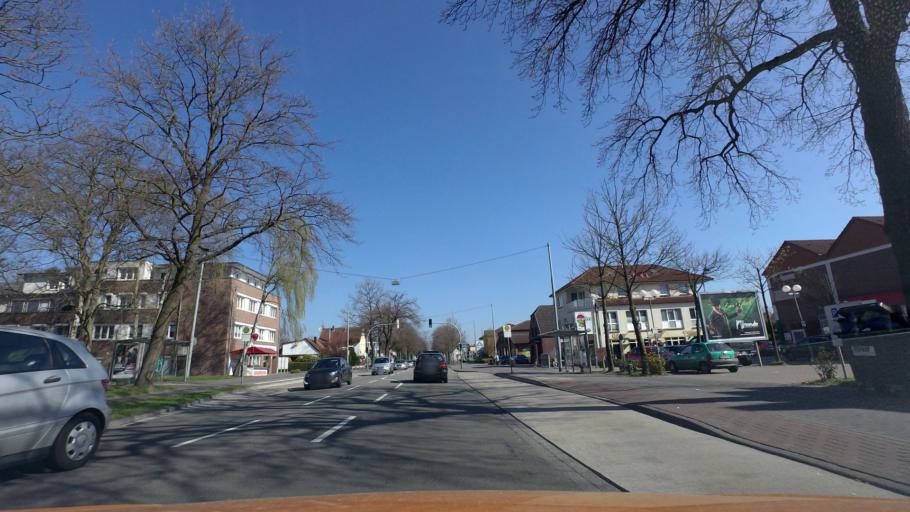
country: DE
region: Lower Saxony
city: Oldenburg
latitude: 53.1129
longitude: 8.2115
